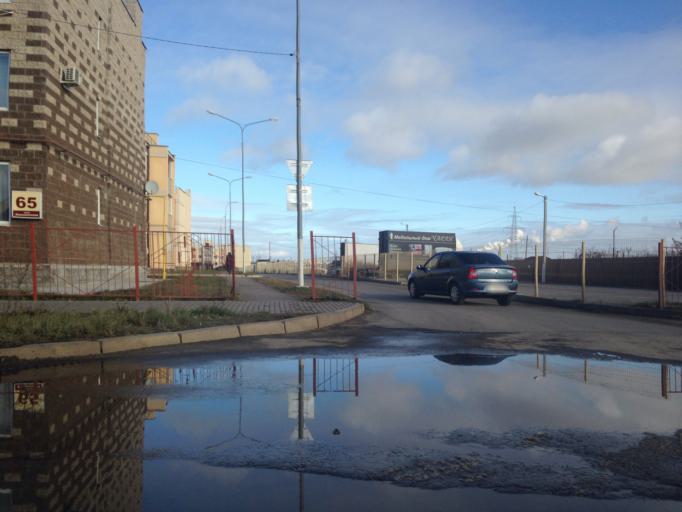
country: RU
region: Ulyanovsk
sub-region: Ulyanovskiy Rayon
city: Ulyanovsk
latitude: 54.2803
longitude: 48.2743
